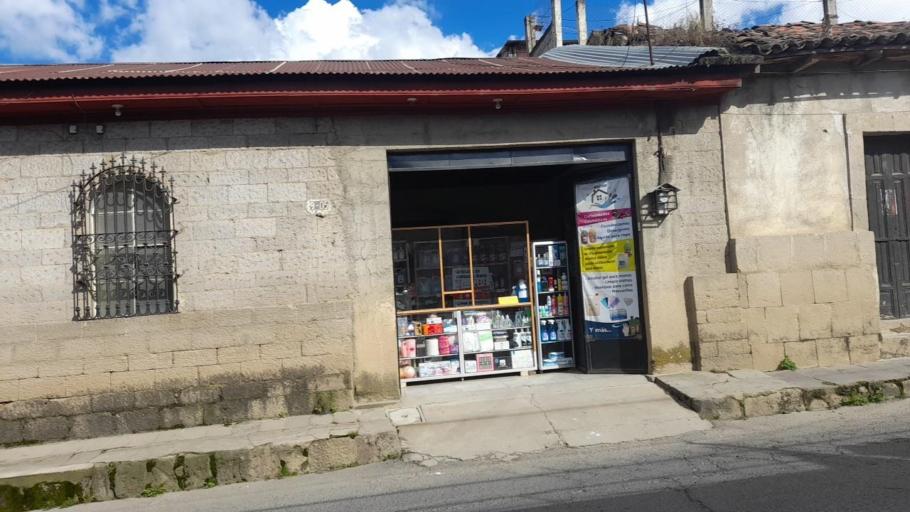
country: GT
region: Quetzaltenango
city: Quetzaltenango
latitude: 14.8312
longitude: -91.5161
